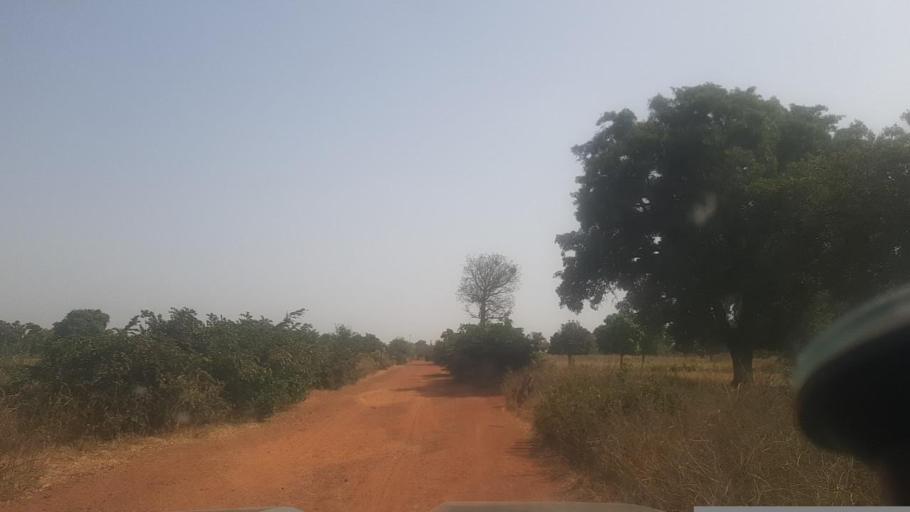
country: ML
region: Segou
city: Bla
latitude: 12.9153
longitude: -6.2509
